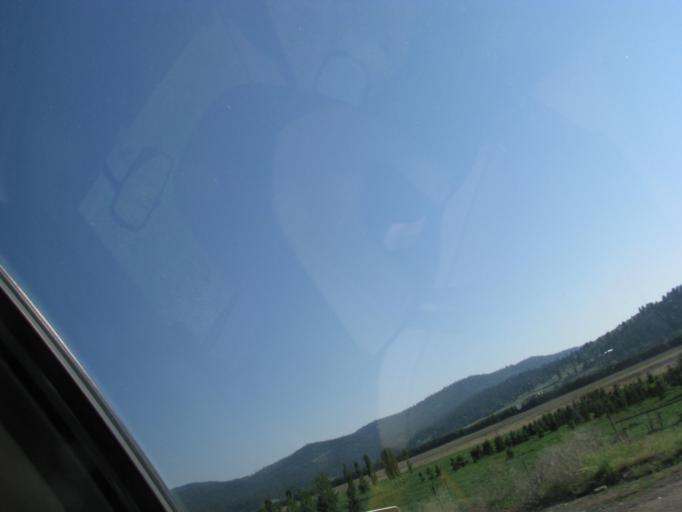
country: US
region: Washington
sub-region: Spokane County
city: Liberty Lake
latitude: 47.6309
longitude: -117.1224
